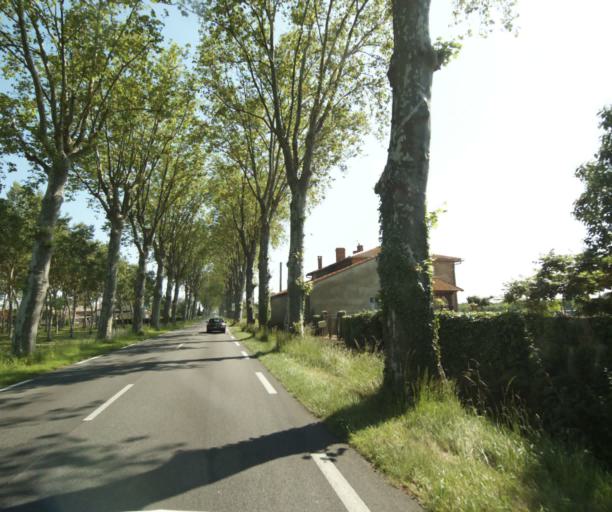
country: FR
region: Midi-Pyrenees
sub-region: Departement du Tarn-et-Garonne
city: Montbeton
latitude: 43.9920
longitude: 1.3119
